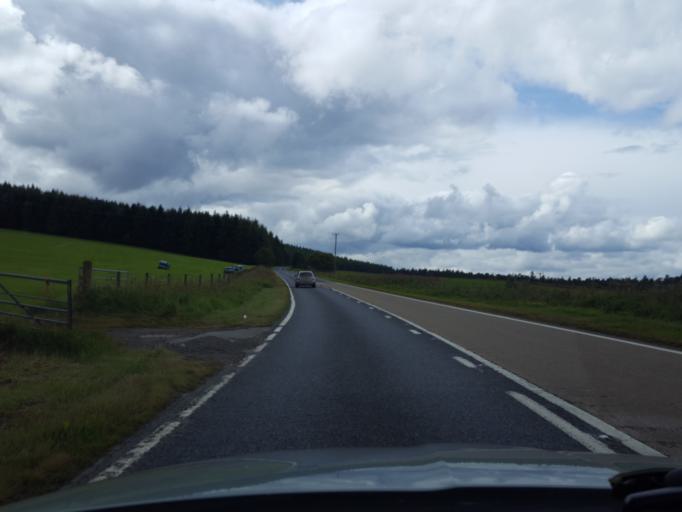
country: GB
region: Scotland
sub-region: Moray
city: Rothes
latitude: 57.4089
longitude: -3.3838
